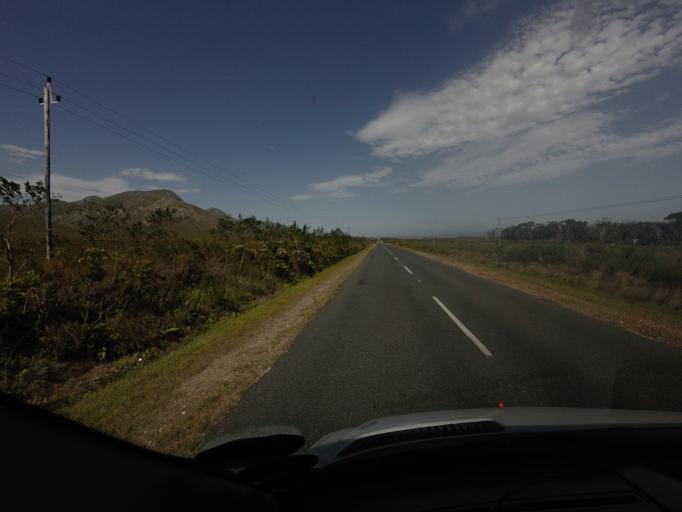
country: ZA
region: Western Cape
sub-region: Overberg District Municipality
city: Hermanus
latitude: -34.4063
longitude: 19.3848
